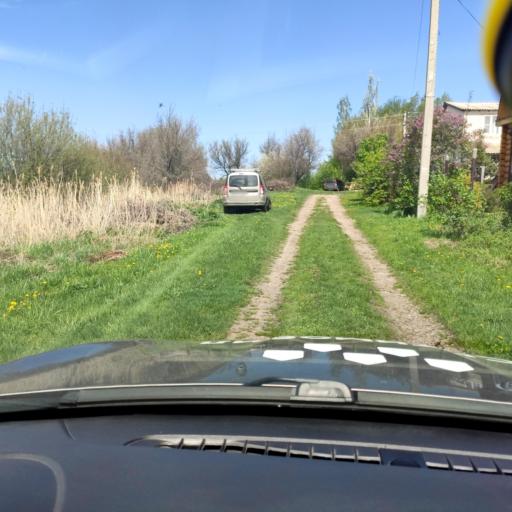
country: RU
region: Samara
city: Tol'yatti
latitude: 53.7025
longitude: 49.4343
